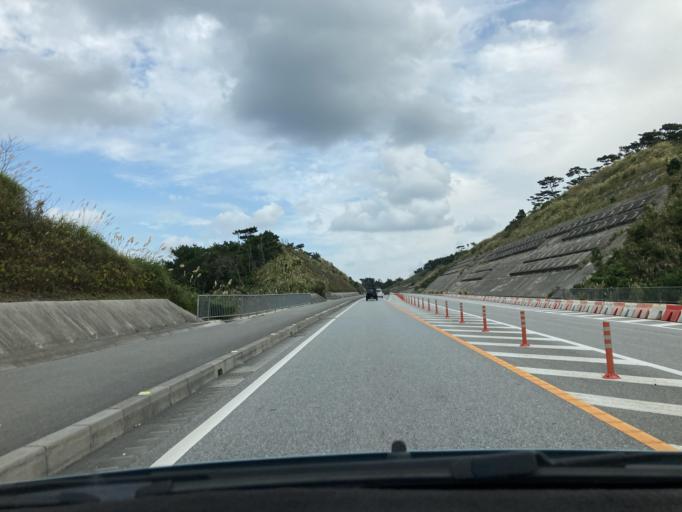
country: JP
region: Okinawa
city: Ishikawa
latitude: 26.4696
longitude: 127.8344
